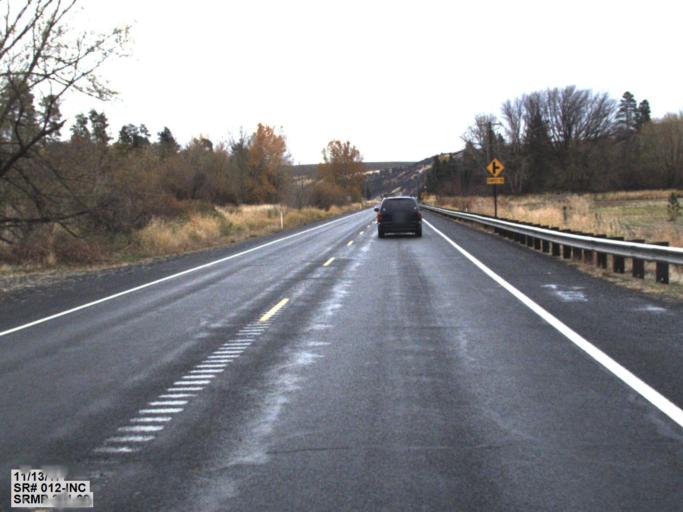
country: US
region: Washington
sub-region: Walla Walla County
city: Waitsburg
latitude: 46.2883
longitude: -118.0772
